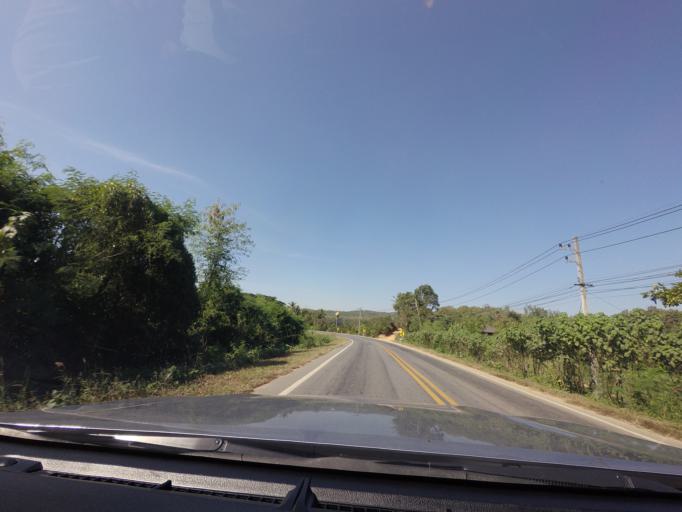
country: TH
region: Sukhothai
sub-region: Amphoe Si Satchanalai
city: Si Satchanalai
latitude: 17.6276
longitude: 99.7010
